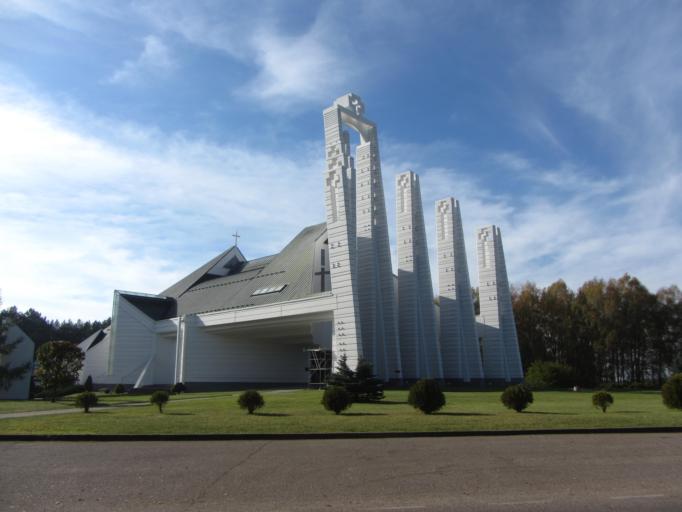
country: LT
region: Vilnius County
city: Elektrenai
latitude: 54.7827
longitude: 24.6817
